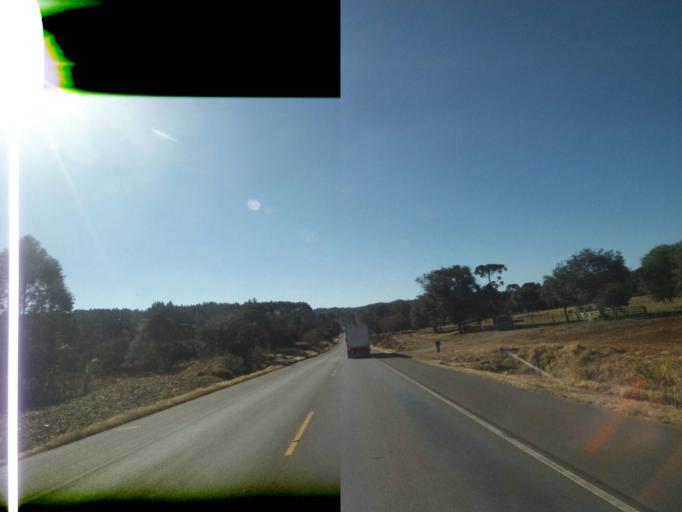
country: BR
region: Parana
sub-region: Tibagi
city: Tibagi
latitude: -24.5917
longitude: -50.4371
